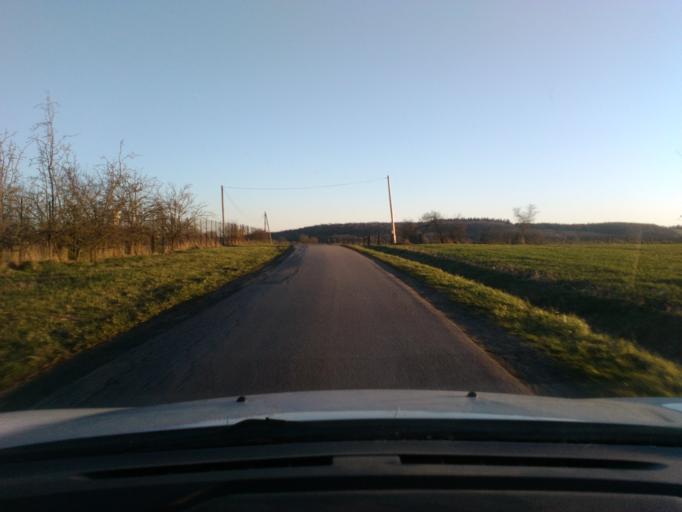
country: FR
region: Lorraine
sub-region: Departement des Vosges
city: Mirecourt
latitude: 48.2945
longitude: 6.1039
